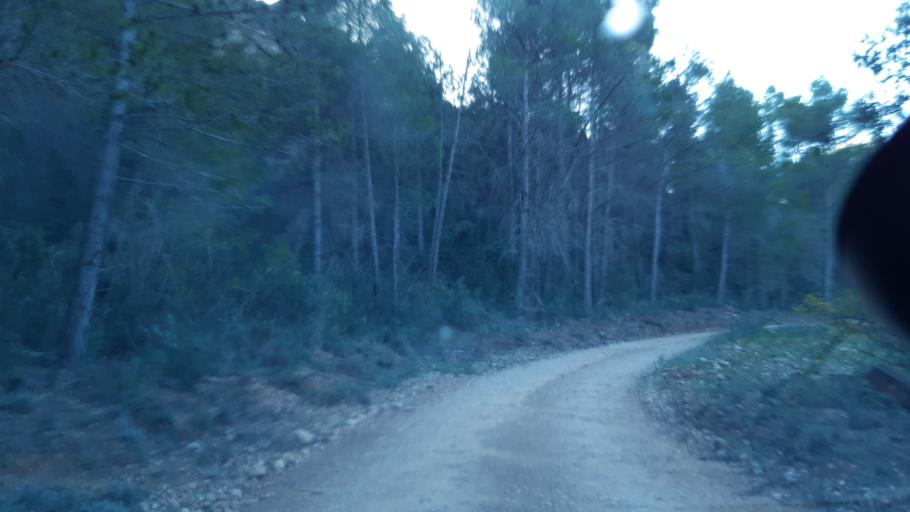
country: ES
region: Aragon
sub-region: Provincia de Teruel
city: Lledo
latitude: 40.8648
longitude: 0.2552
